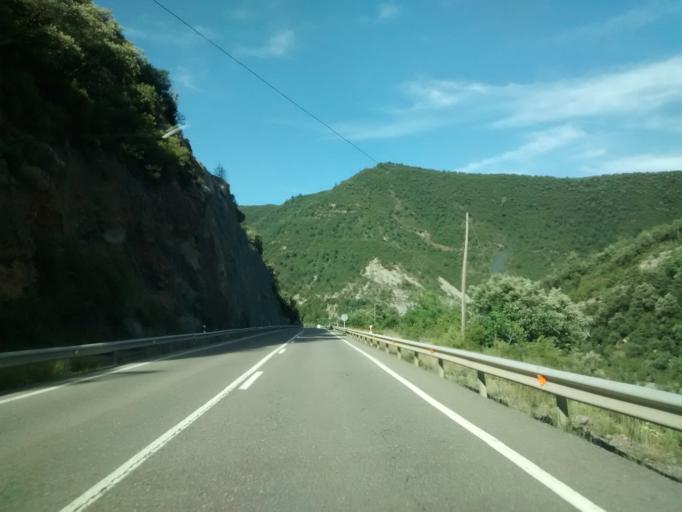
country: ES
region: Aragon
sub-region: Provincia de Huesca
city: Boltana
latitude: 42.4638
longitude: 0.0417
